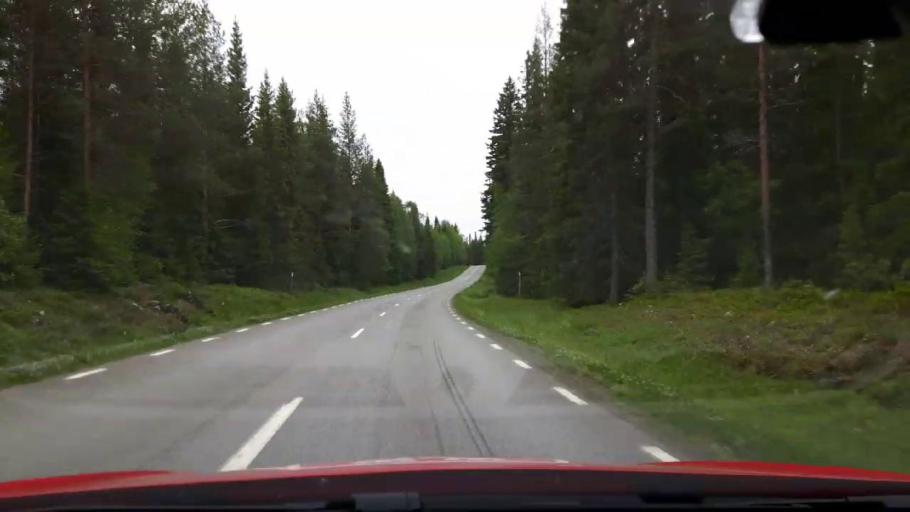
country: SE
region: Jaemtland
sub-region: Stroemsunds Kommun
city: Stroemsund
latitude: 63.4511
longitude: 15.4678
